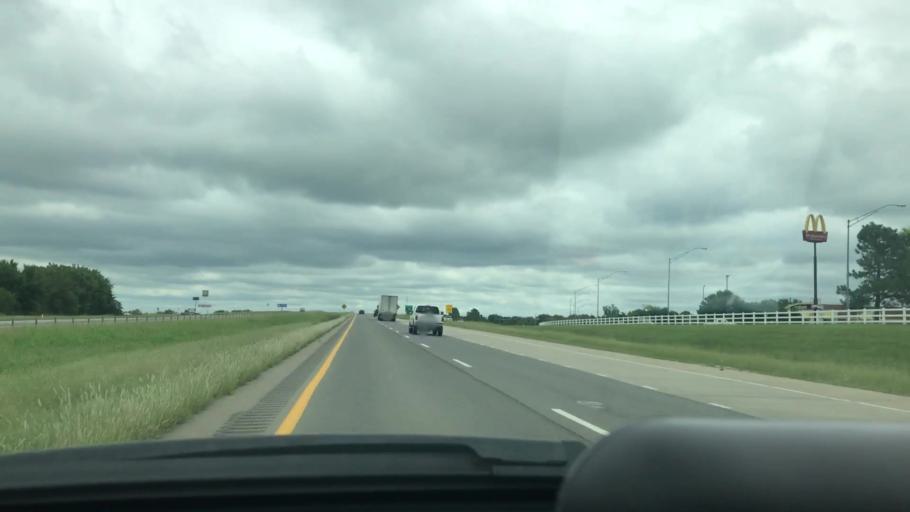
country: US
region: Oklahoma
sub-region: McIntosh County
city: Checotah
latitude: 35.4707
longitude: -95.5382
